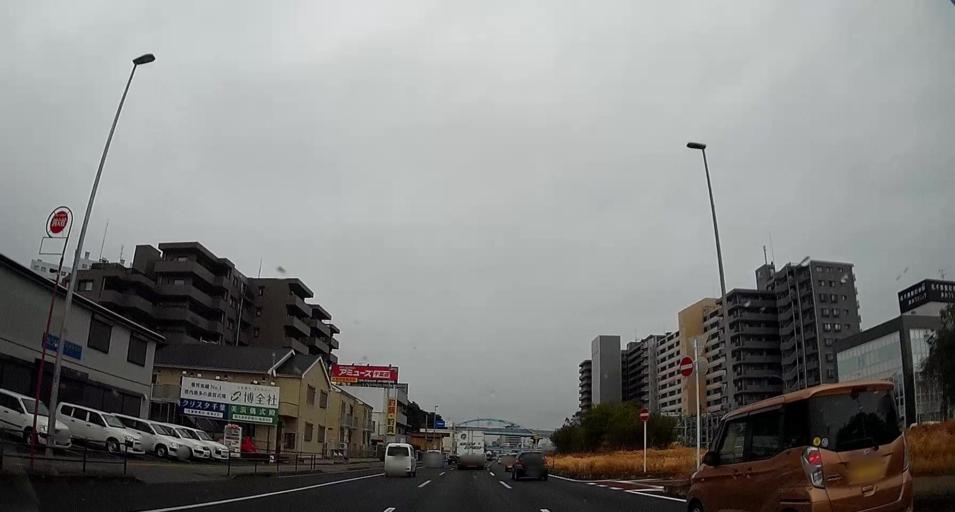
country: JP
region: Chiba
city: Chiba
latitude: 35.6347
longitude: 140.0821
